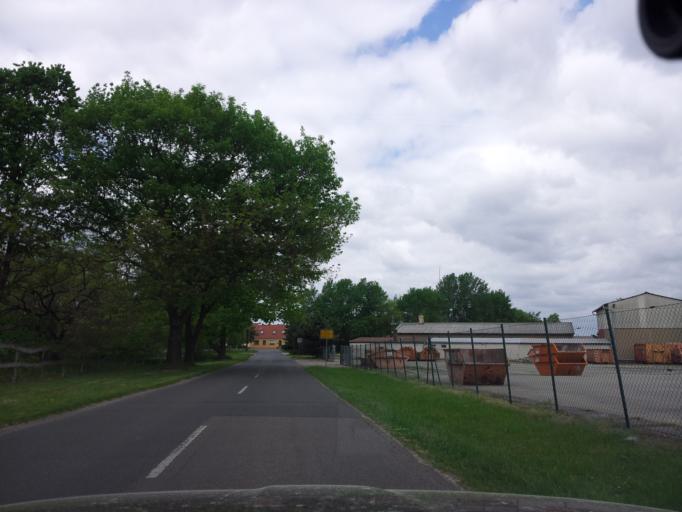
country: DE
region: Brandenburg
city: Treuenbrietzen
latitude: 52.0743
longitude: 12.8113
